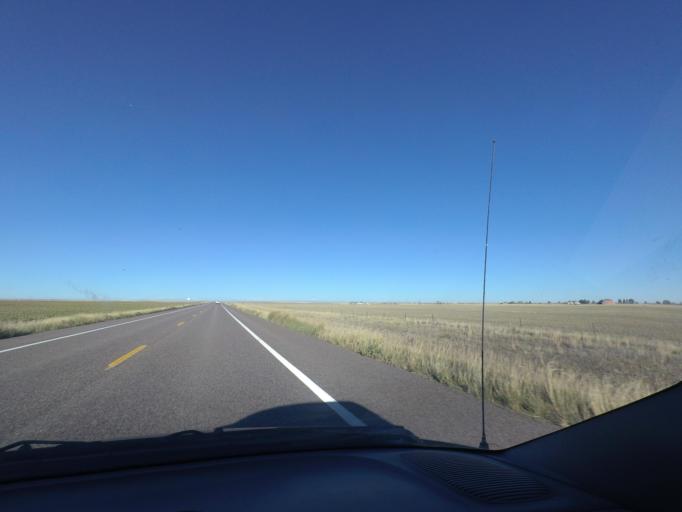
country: US
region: Colorado
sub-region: Arapahoe County
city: Byers
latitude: 39.7396
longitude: -104.1581
